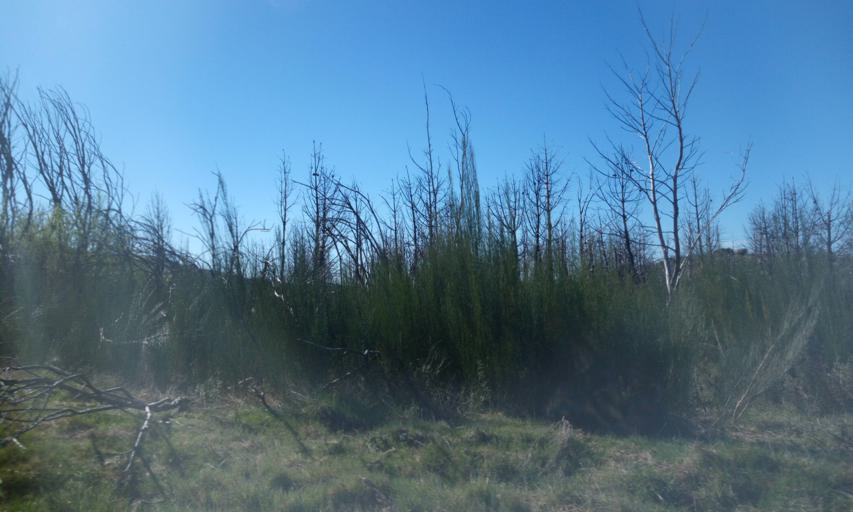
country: PT
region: Guarda
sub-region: Manteigas
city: Manteigas
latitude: 40.4892
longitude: -7.5664
